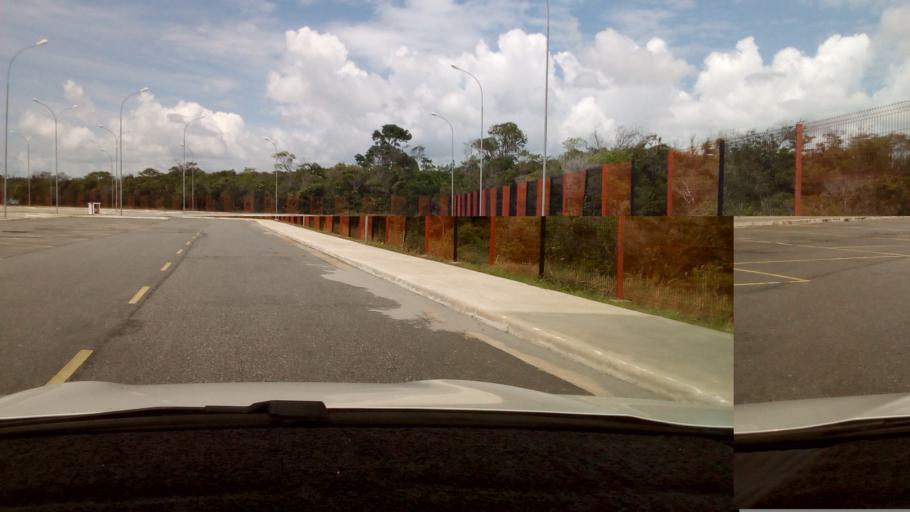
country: BR
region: Paraiba
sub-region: Joao Pessoa
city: Joao Pessoa
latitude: -7.1866
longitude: -34.8055
